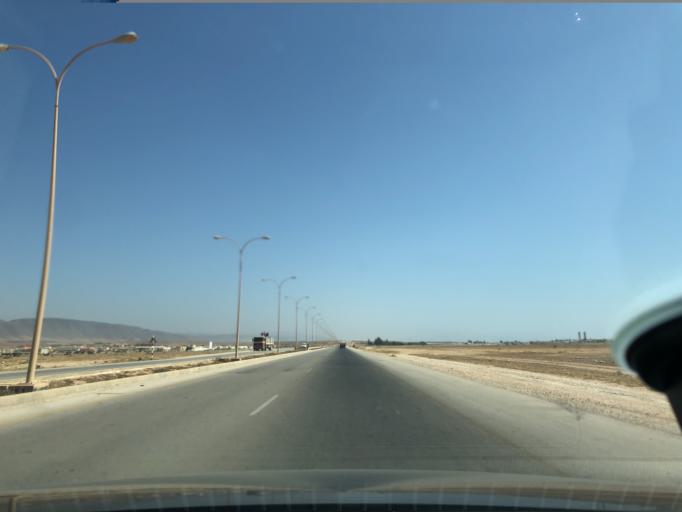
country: OM
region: Zufar
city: Salalah
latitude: 17.0527
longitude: 54.2843
